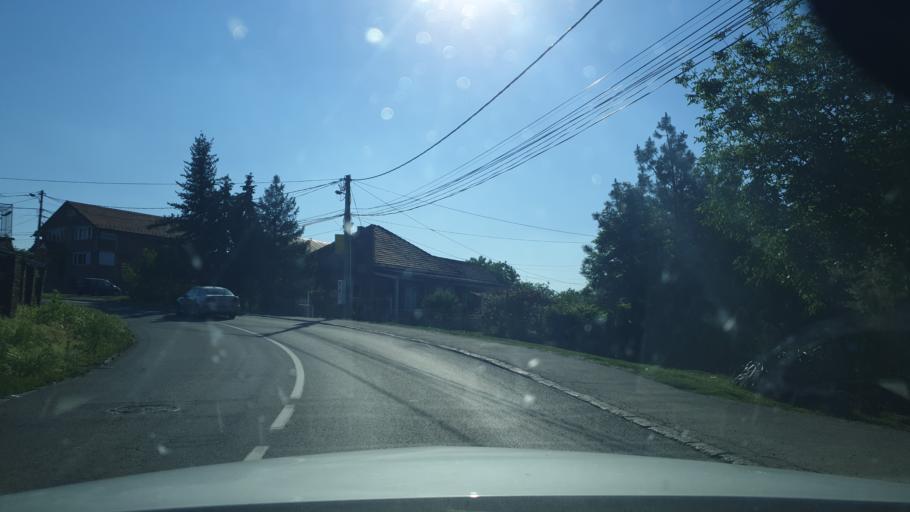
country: RS
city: Ostruznica
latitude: 44.7225
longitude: 20.3669
